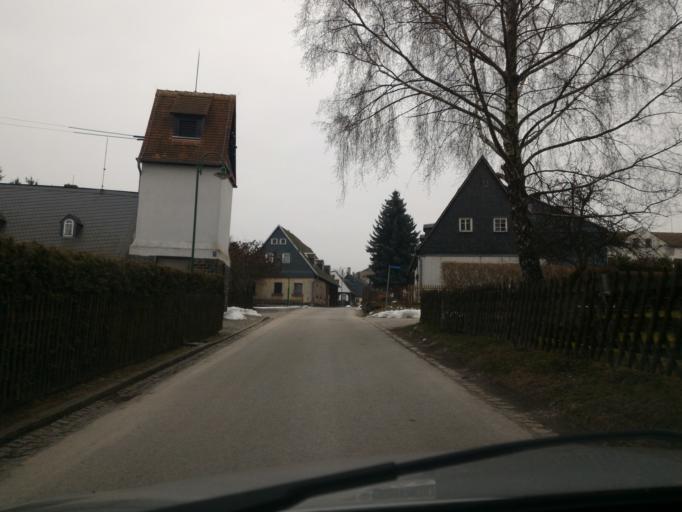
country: DE
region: Saxony
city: Neugersdorf
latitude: 50.9756
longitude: 14.6006
